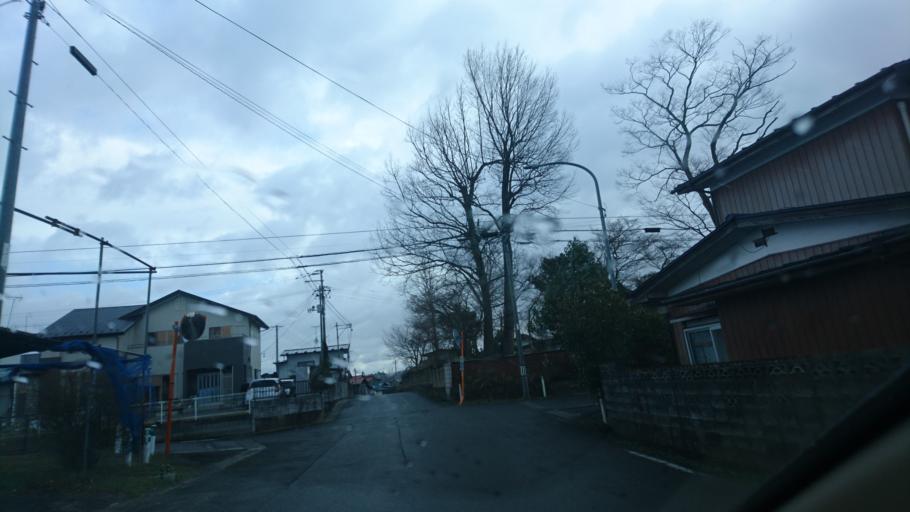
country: JP
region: Iwate
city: Ichinoseki
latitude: 38.7741
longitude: 141.0272
